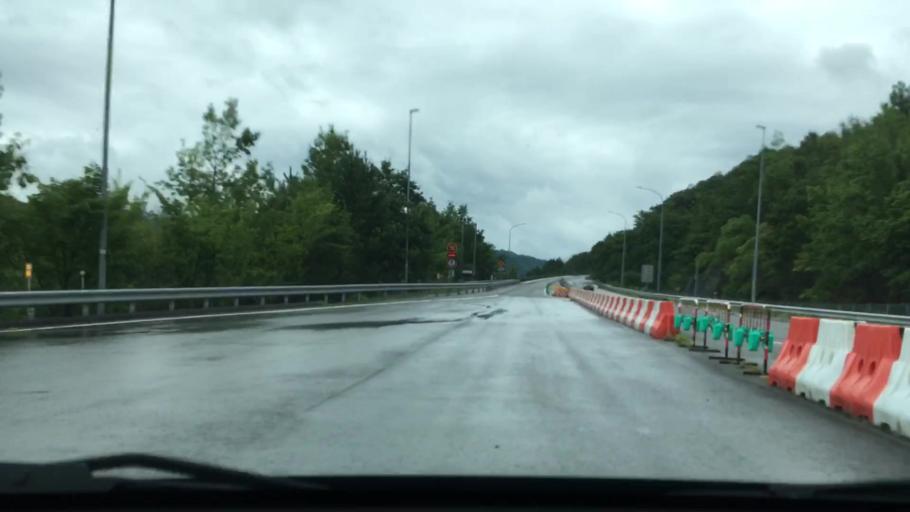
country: JP
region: Hyogo
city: Toyooka
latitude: 35.2858
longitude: 134.8219
